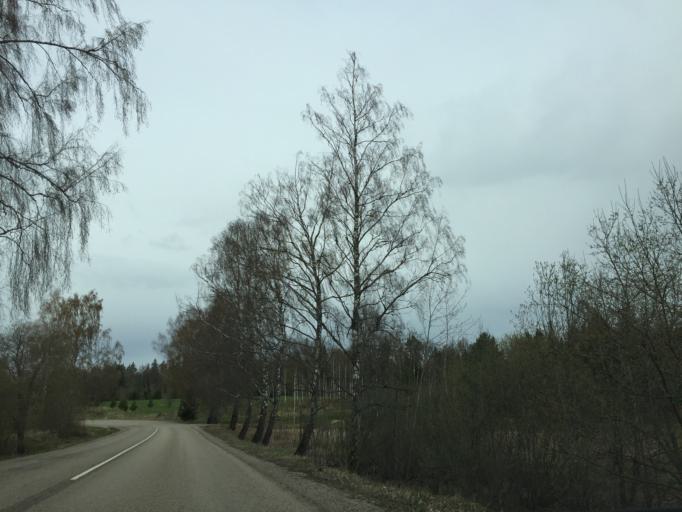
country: LV
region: Amatas Novads
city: Drabesi
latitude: 57.2574
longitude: 25.2758
